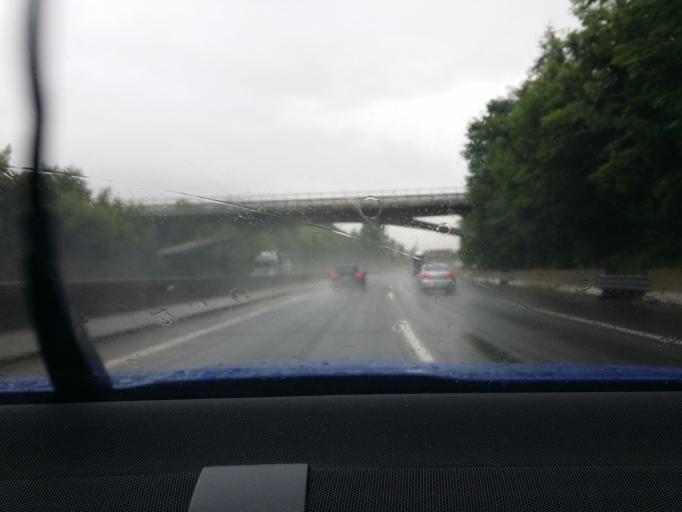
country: AT
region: Salzburg
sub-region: Politischer Bezirk Hallein
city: Kuchl
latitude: 47.6304
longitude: 13.1317
